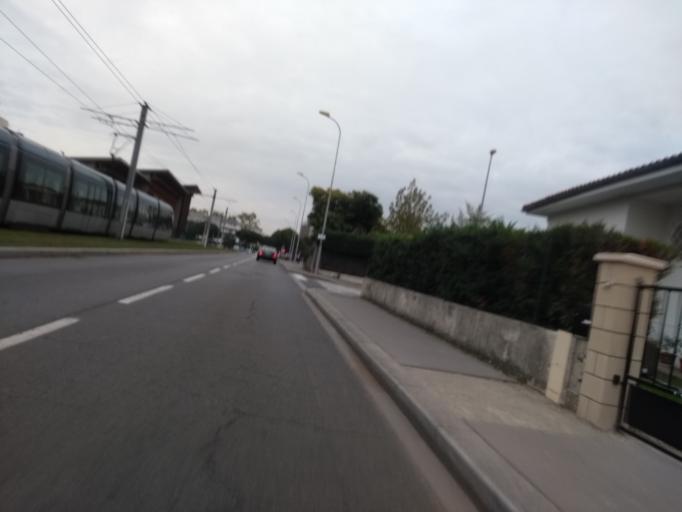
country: FR
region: Aquitaine
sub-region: Departement de la Gironde
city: Talence
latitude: 44.8061
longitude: -0.5956
